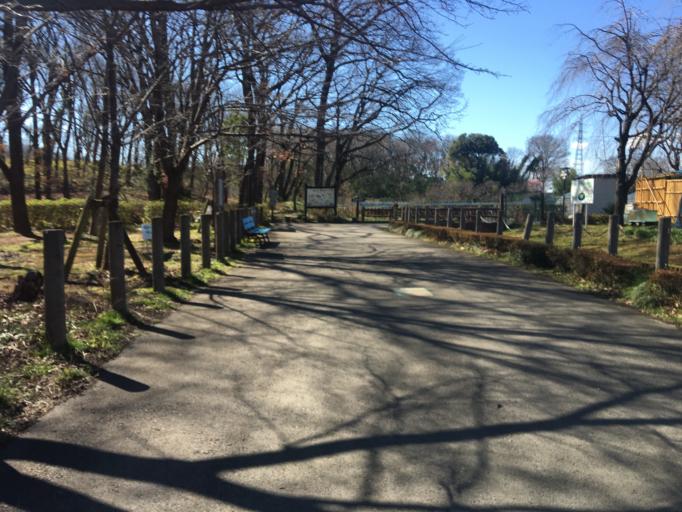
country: JP
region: Saitama
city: Asaka
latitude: 35.7948
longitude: 139.5581
